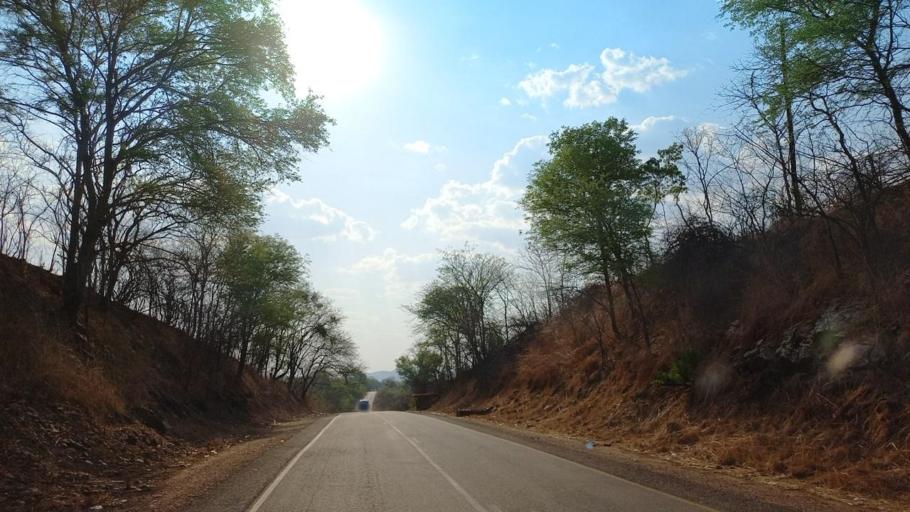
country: ZM
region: Lusaka
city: Luangwa
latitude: -14.9819
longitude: 30.1405
